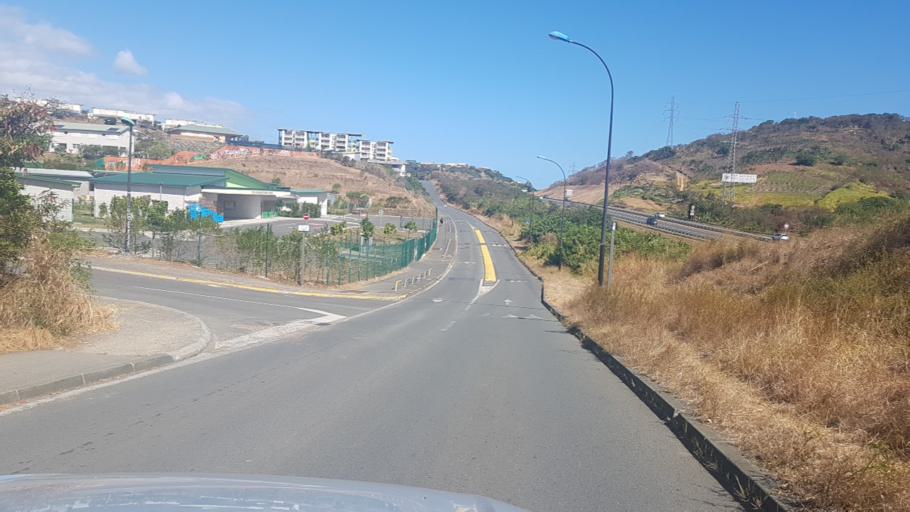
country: NC
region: South Province
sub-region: Dumbea
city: Dumbea
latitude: -22.1968
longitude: 166.4485
